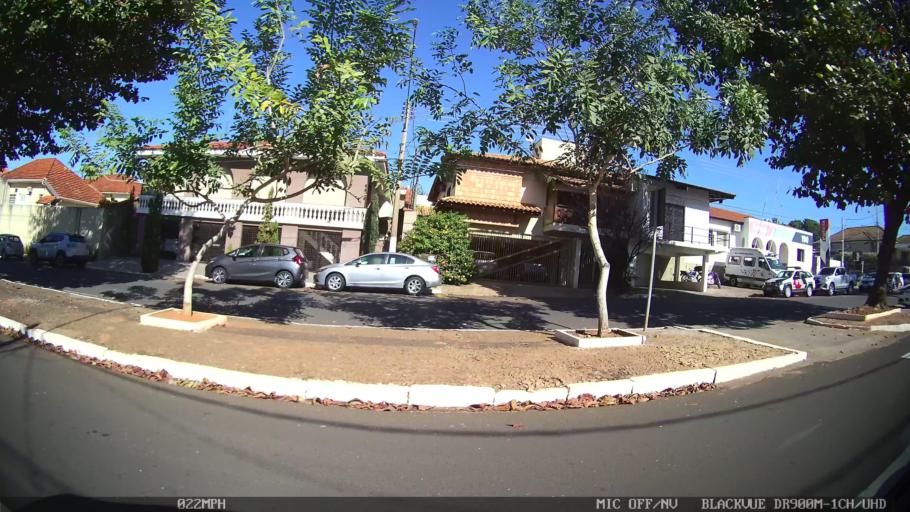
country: BR
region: Sao Paulo
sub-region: Olimpia
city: Olimpia
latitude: -20.7417
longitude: -48.9156
